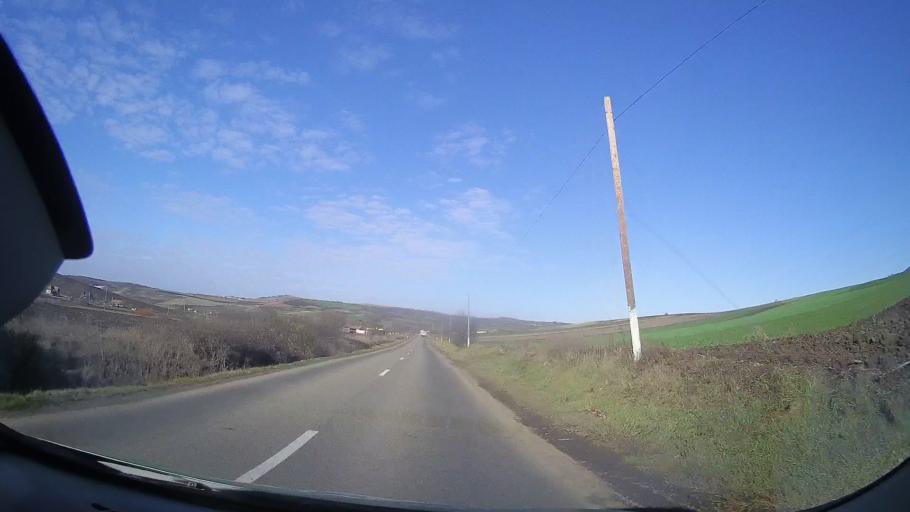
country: RO
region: Mures
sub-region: Comuna Grebenisu de Campie
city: Grebenisu de Campie
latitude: 46.6056
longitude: 24.3412
